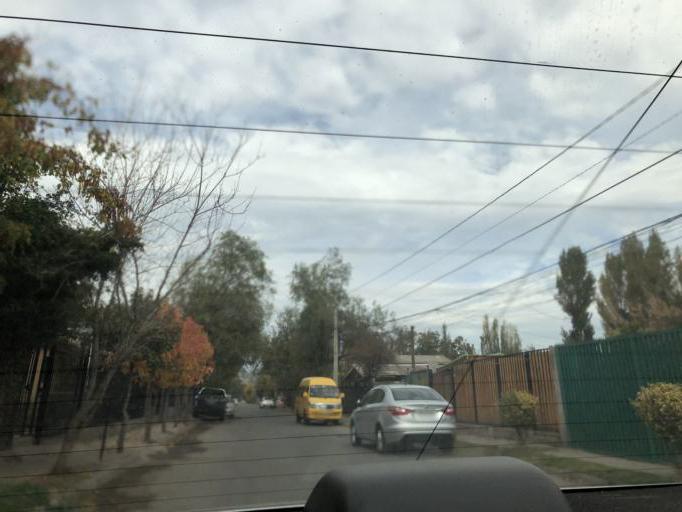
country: CL
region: Santiago Metropolitan
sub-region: Provincia de Cordillera
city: Puente Alto
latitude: -33.6096
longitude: -70.5332
